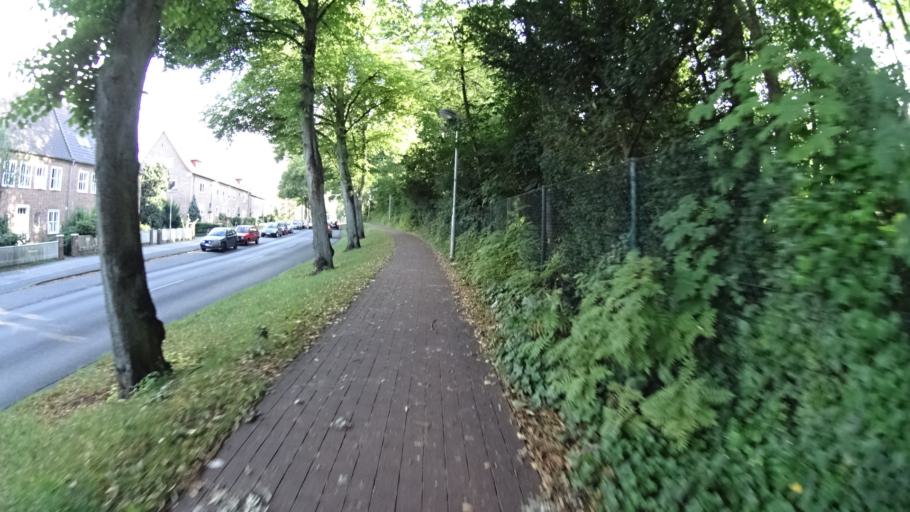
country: DE
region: Lower Saxony
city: Lueneburg
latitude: 53.2344
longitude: 10.3968
